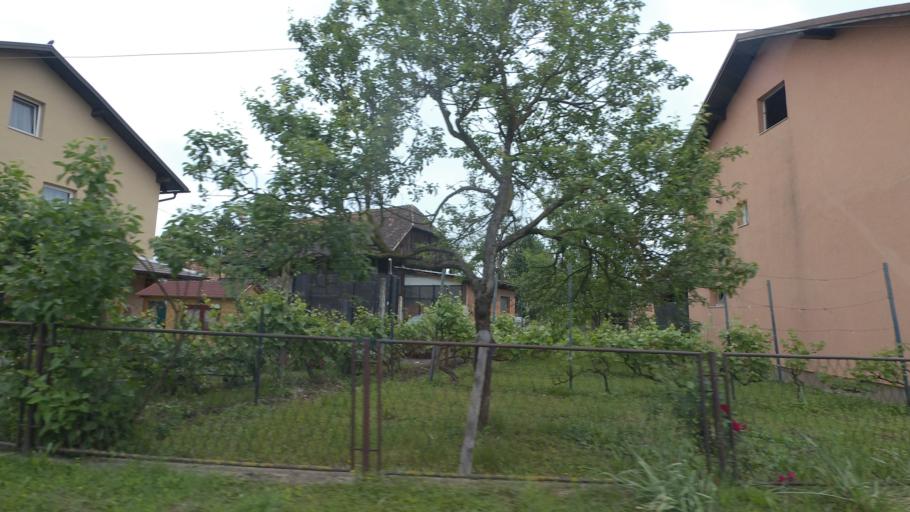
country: HR
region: Karlovacka
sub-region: Grad Karlovac
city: Karlovac
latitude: 45.4094
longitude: 15.5997
